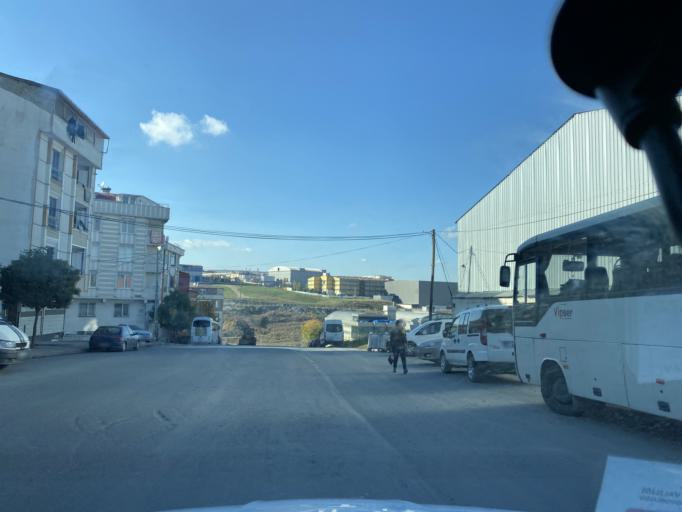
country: TR
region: Istanbul
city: Esenyurt
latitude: 41.0477
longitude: 28.6467
